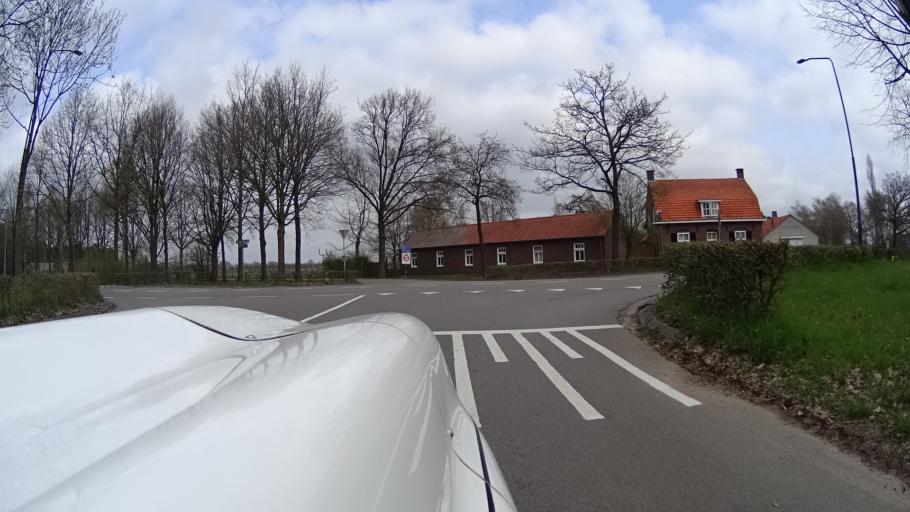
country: NL
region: North Brabant
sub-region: Gemeente Son en Breugel
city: Breugel
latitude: 51.5204
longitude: 5.5234
